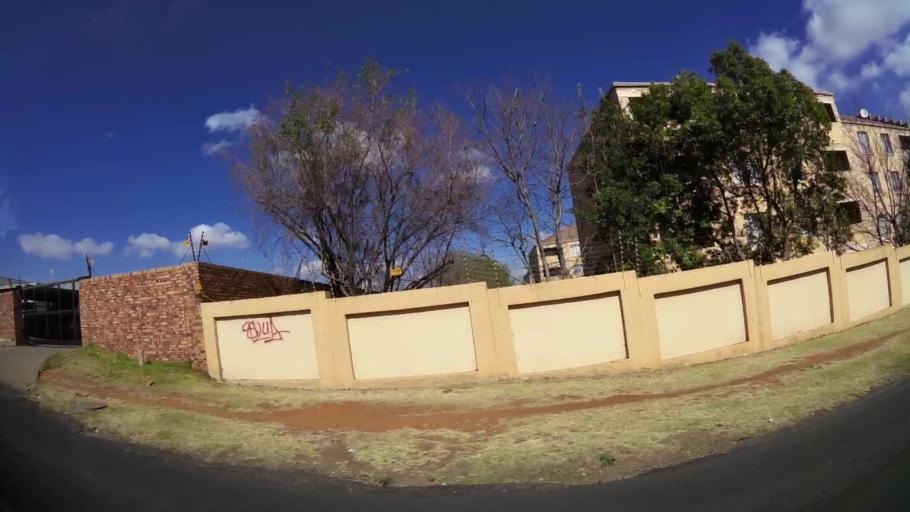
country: ZA
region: Gauteng
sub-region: City of Johannesburg Metropolitan Municipality
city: Roodepoort
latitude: -26.1255
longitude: 27.8446
